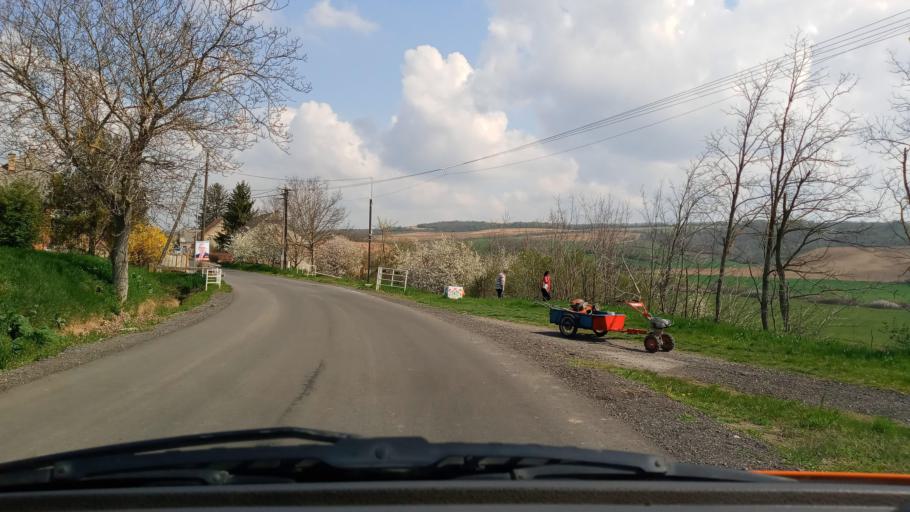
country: HU
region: Baranya
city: Pecsvarad
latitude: 46.0967
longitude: 18.4719
